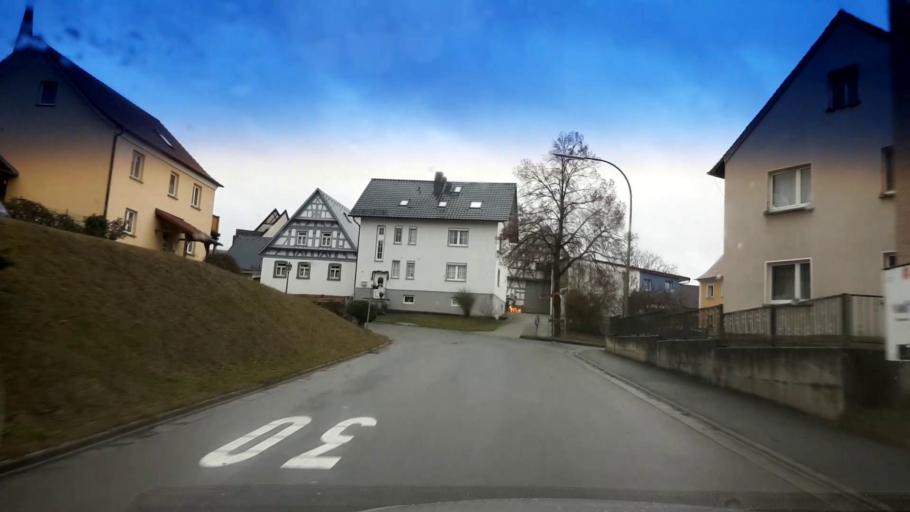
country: DE
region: Bavaria
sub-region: Upper Franconia
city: Litzendorf
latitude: 49.8718
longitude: 11.0442
